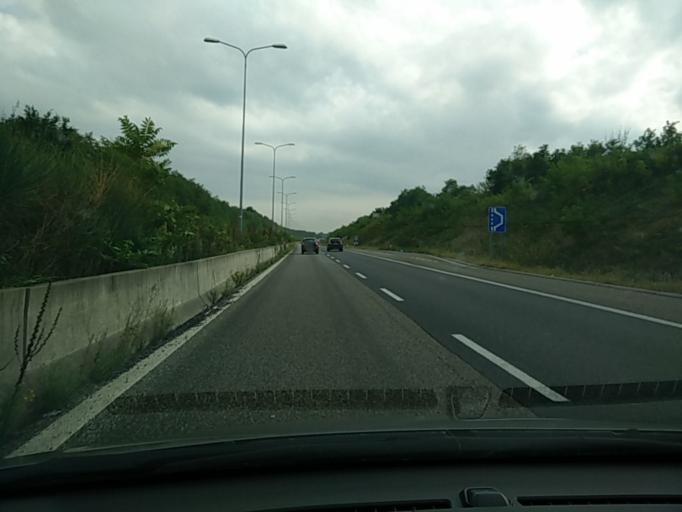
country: IT
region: Lombardy
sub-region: Provincia di Varese
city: Vizzola Ticino
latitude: 45.6033
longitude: 8.7118
